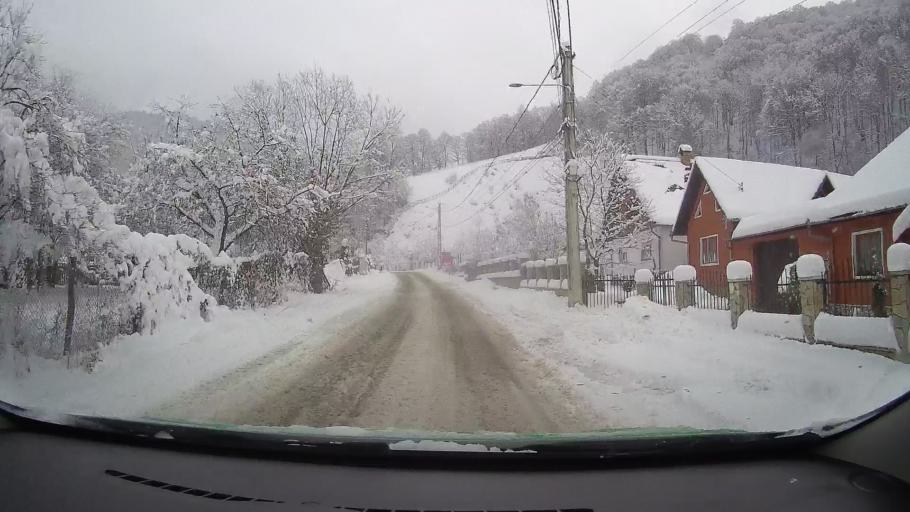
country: RO
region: Alba
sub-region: Comuna Sugag
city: Dobra
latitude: 45.7630
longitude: 23.6526
